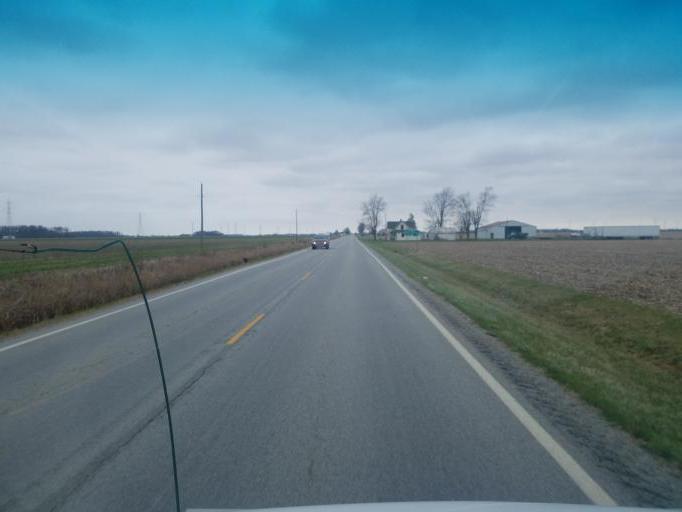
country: US
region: Ohio
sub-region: Van Wert County
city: Van Wert
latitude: 40.9320
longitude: -84.4715
